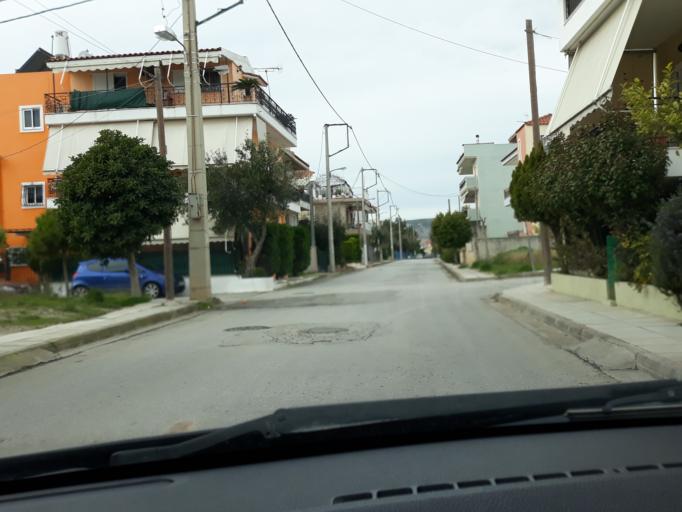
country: GR
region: Attica
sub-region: Nomarchia Anatolikis Attikis
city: Acharnes
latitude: 38.0855
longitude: 23.7181
